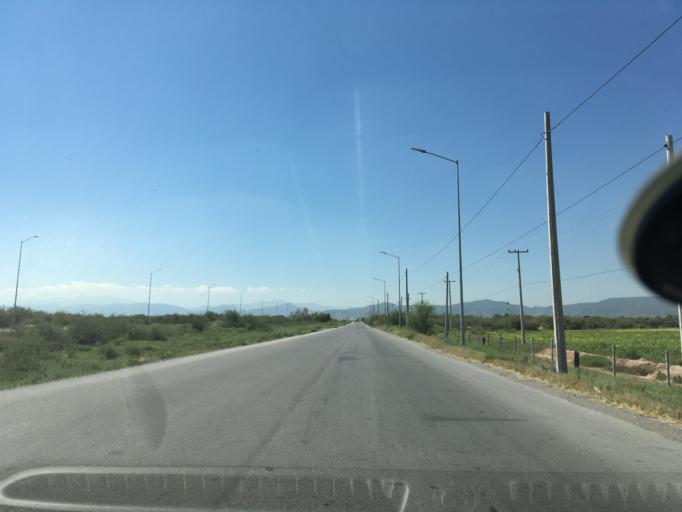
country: MX
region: Coahuila
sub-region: Torreon
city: Fraccionamiento la Noria
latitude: 25.5110
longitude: -103.3202
